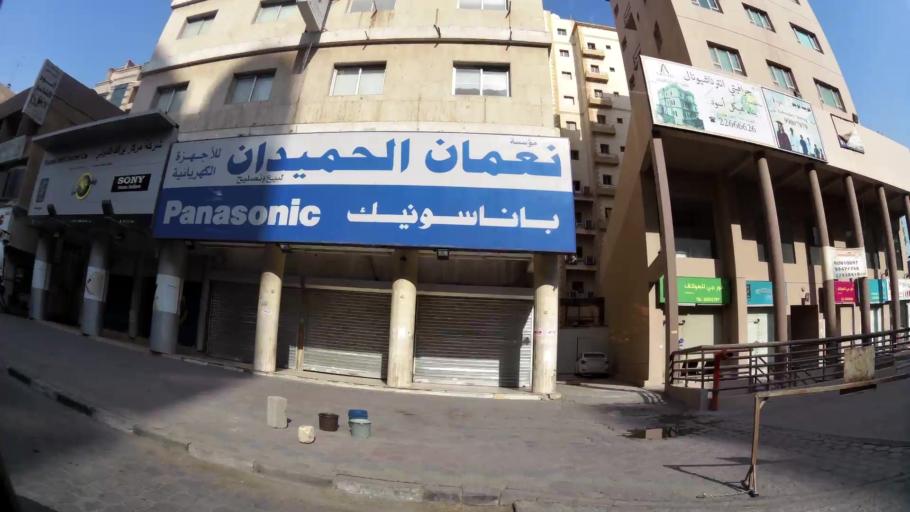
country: KW
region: Muhafazat Hawalli
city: Hawalli
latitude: 29.3437
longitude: 48.0139
